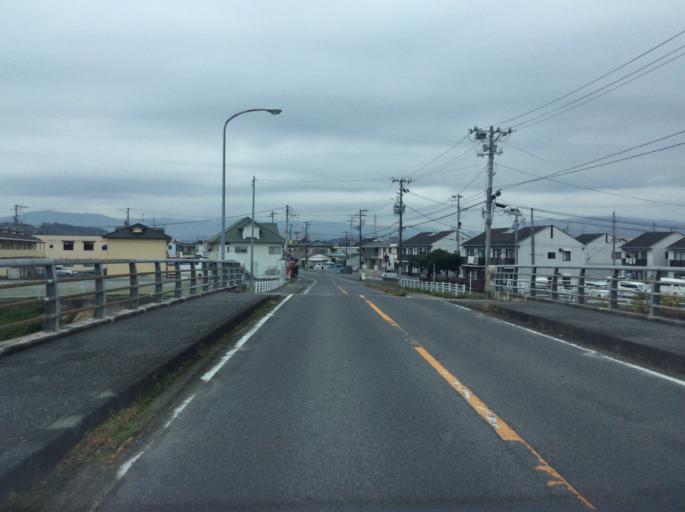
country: JP
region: Fukushima
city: Iwaki
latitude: 37.0496
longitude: 140.9127
